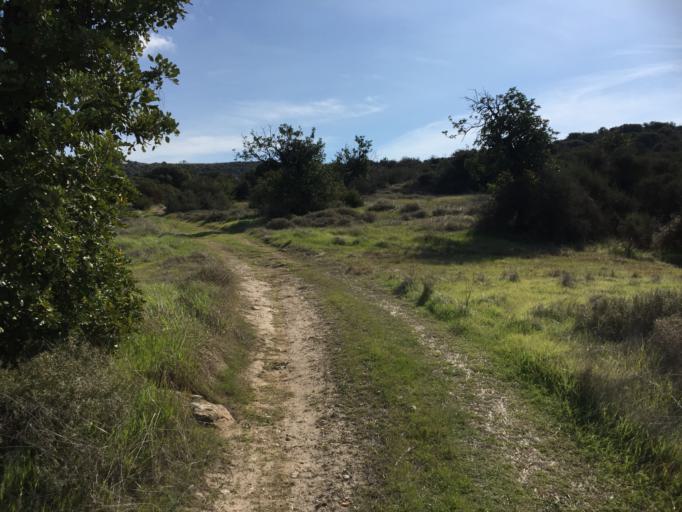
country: CY
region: Limassol
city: Mouttagiaka
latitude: 34.7466
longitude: 33.1124
